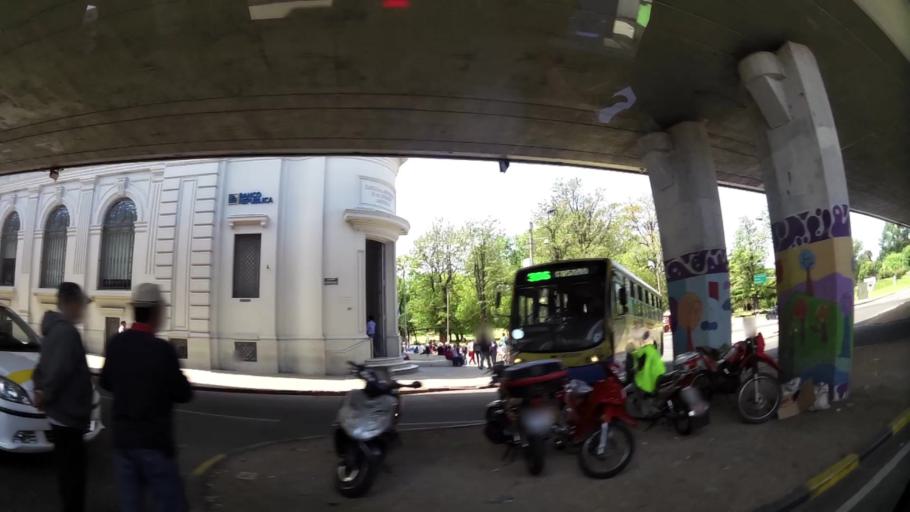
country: UY
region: Montevideo
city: Montevideo
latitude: -34.8609
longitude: -56.2143
